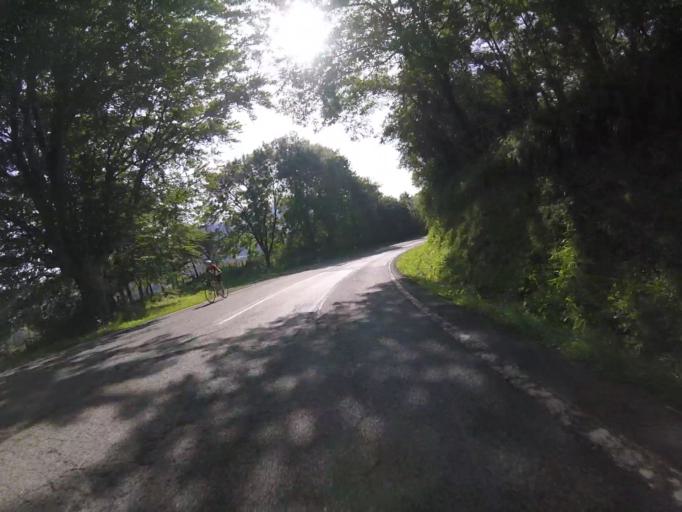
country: ES
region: Navarre
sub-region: Provincia de Navarra
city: Zugarramurdi
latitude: 43.2253
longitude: -1.4916
